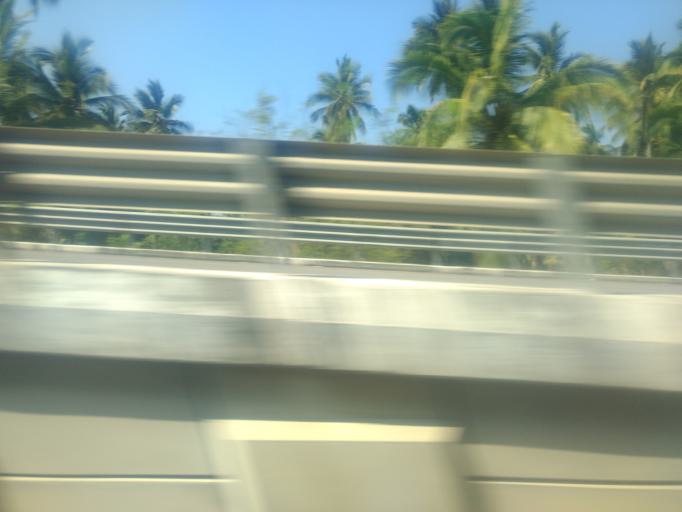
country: MX
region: Colima
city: El Colomo
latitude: 18.9899
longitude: -104.2223
